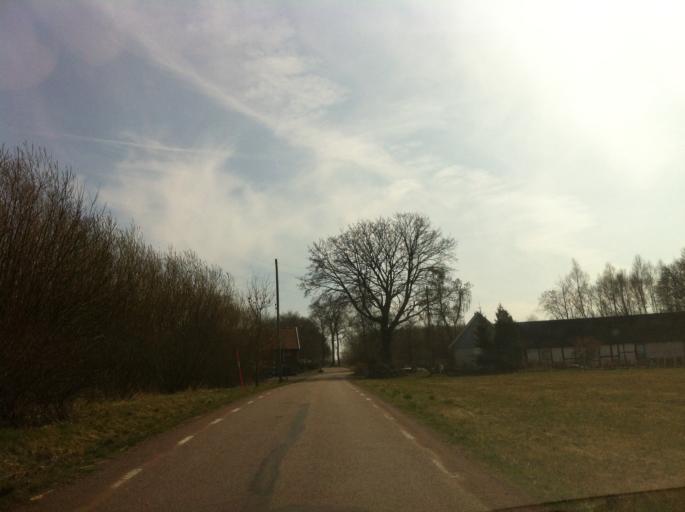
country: SE
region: Skane
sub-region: Klippans Kommun
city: Ljungbyhed
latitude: 55.9951
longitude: 13.2321
